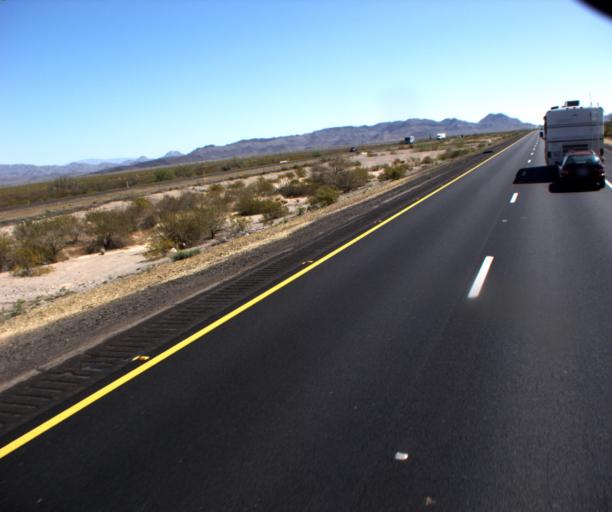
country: US
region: Arizona
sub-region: La Paz County
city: Salome
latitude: 33.6240
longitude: -113.7222
